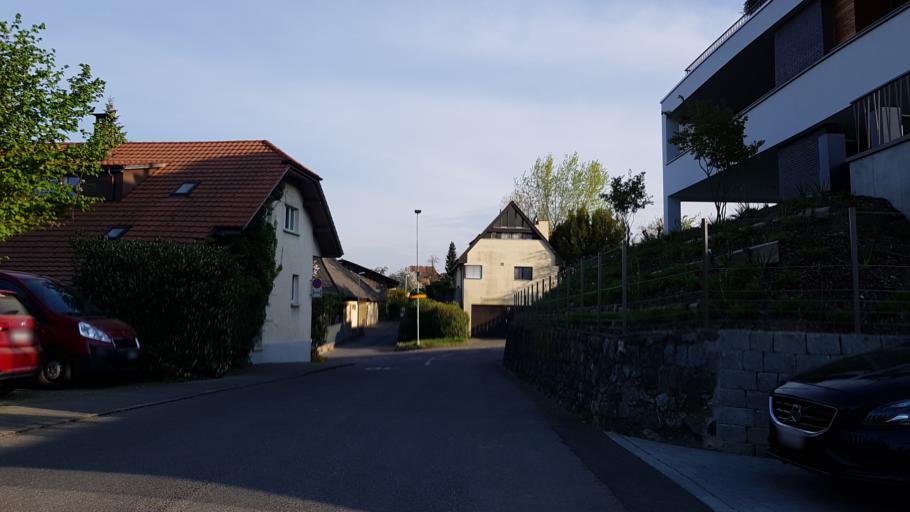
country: CH
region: Aargau
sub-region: Bezirk Kulm
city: Reinach
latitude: 47.2690
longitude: 8.2092
